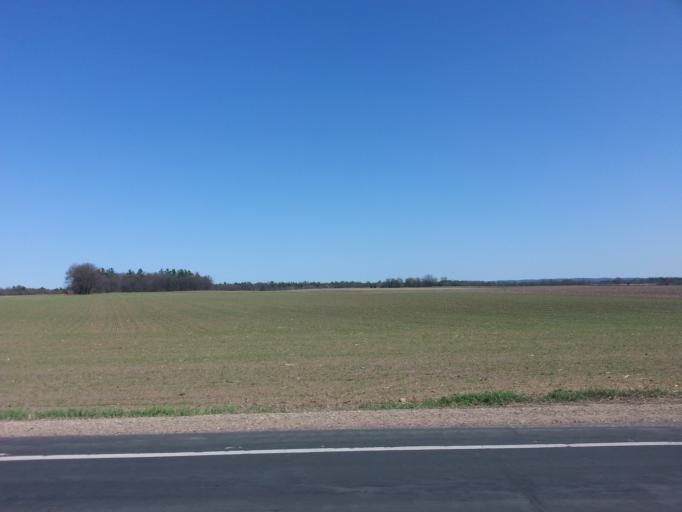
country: US
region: Wisconsin
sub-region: Pepin County
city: Durand
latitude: 44.7092
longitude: -91.9473
